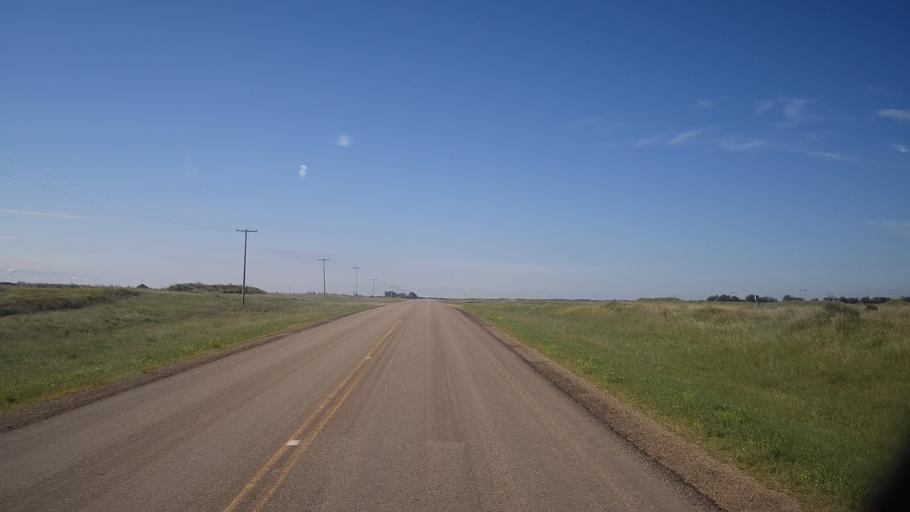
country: CA
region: Saskatchewan
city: Watrous
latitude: 51.7312
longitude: -105.3574
